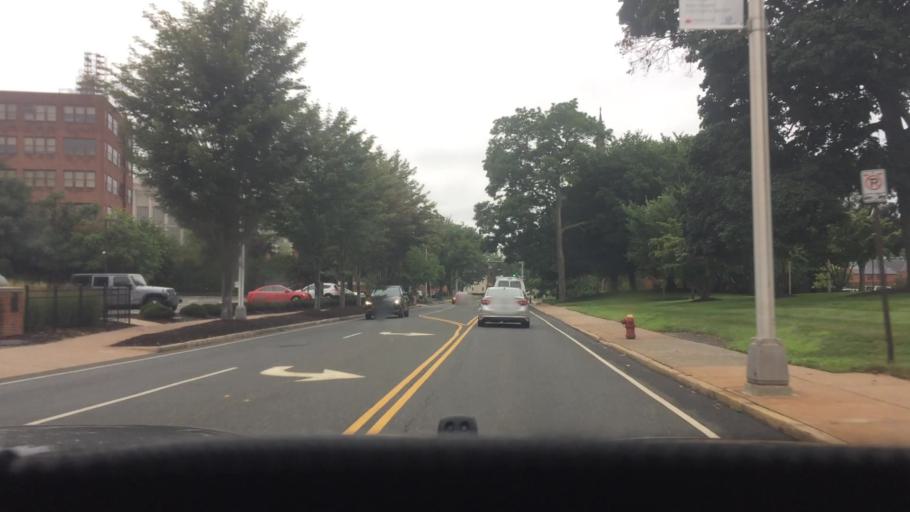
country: US
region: Connecticut
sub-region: Hartford County
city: Hartford
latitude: 41.7689
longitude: -72.6883
